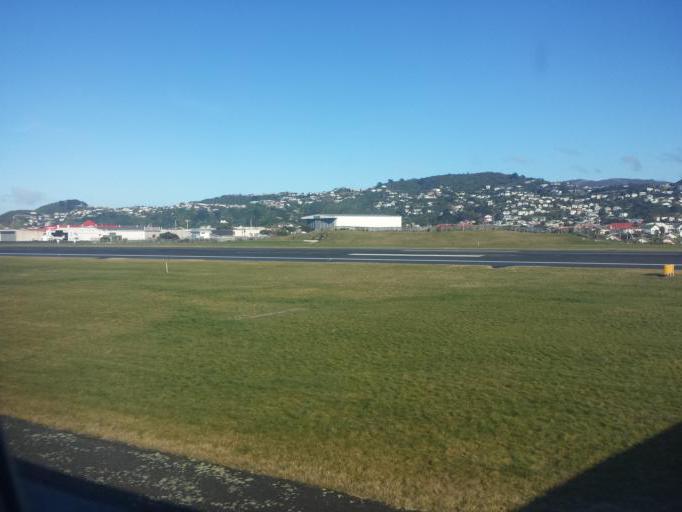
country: NZ
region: Wellington
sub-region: Wellington City
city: Wellington
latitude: -41.3225
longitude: 174.8085
